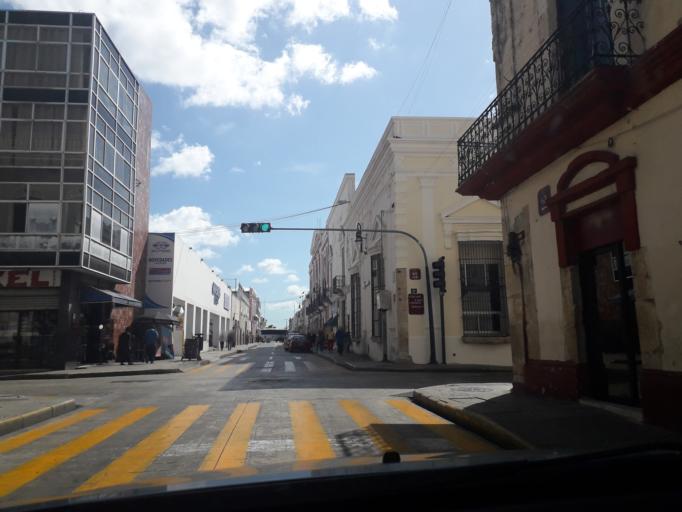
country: MX
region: Yucatan
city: Merida
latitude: 20.9656
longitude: -89.6247
